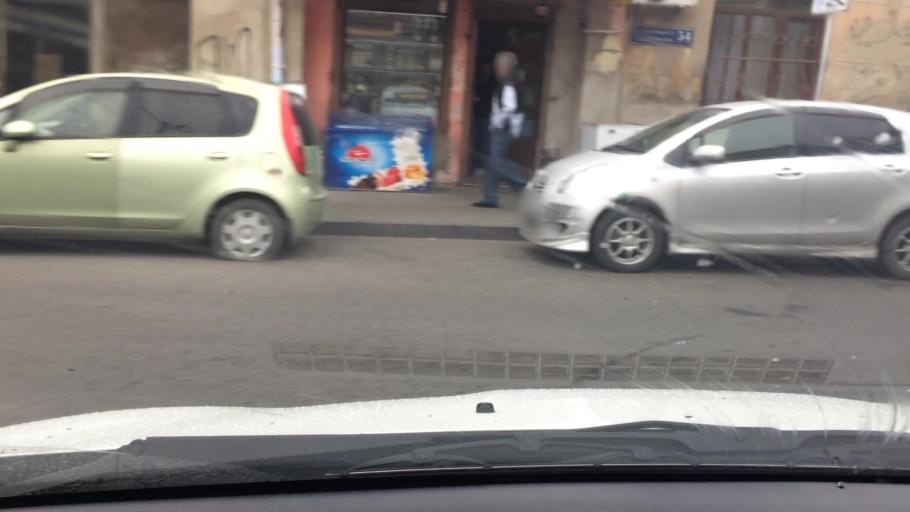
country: GE
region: T'bilisi
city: Tbilisi
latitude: 41.7080
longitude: 44.8029
